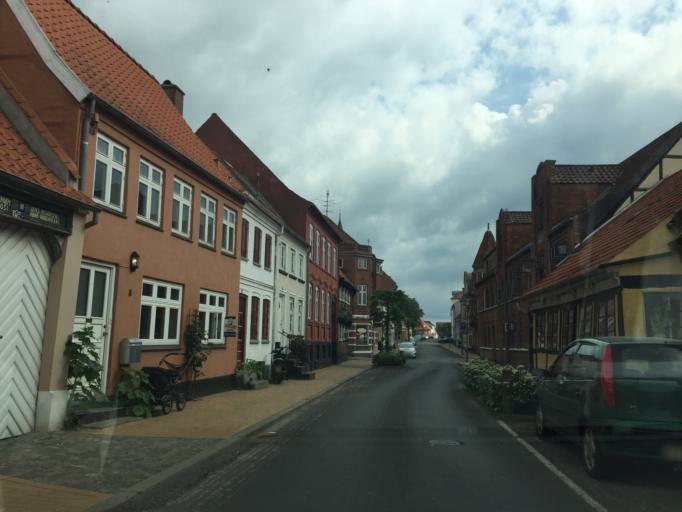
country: DK
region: South Denmark
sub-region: Assens Kommune
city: Assens
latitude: 55.2711
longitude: 9.8928
